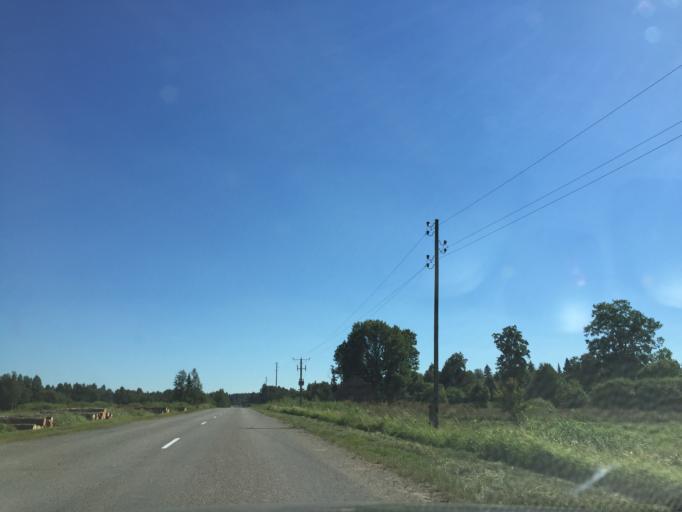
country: LV
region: Akniste
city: Akniste
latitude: 56.0992
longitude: 25.8624
